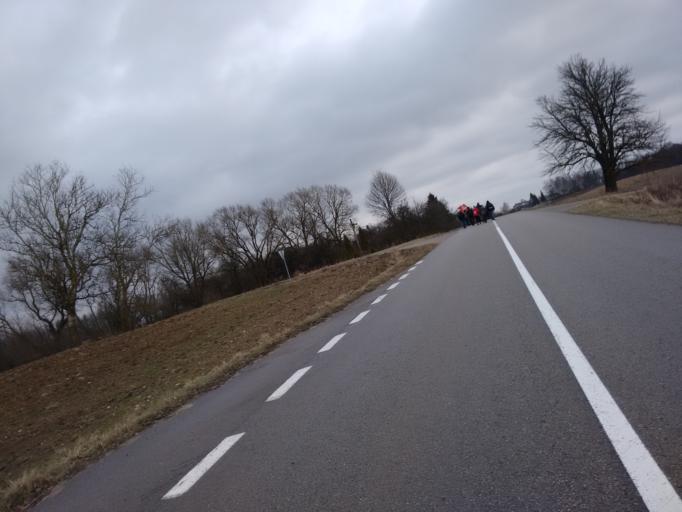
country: LT
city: Veisiejai
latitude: 54.2450
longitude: 23.8717
